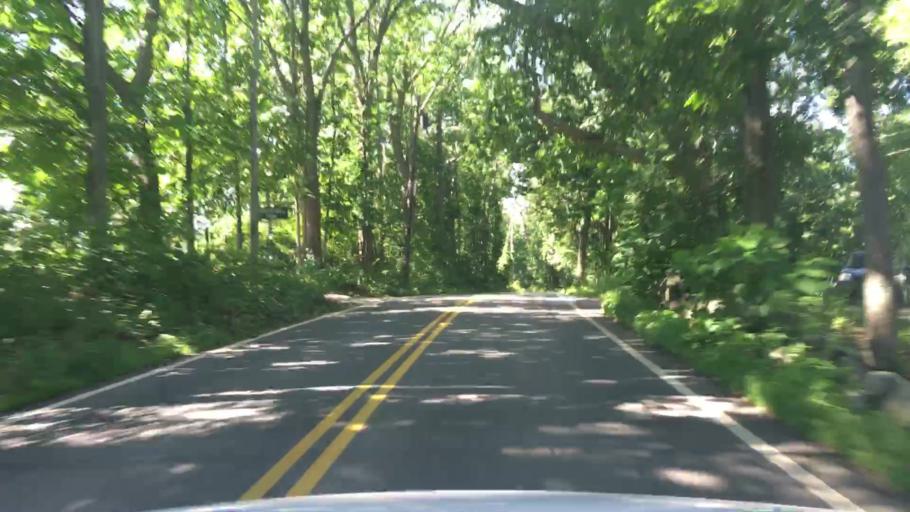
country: US
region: New Hampshire
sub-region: Strafford County
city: Dover
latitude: 43.1797
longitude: -70.8381
